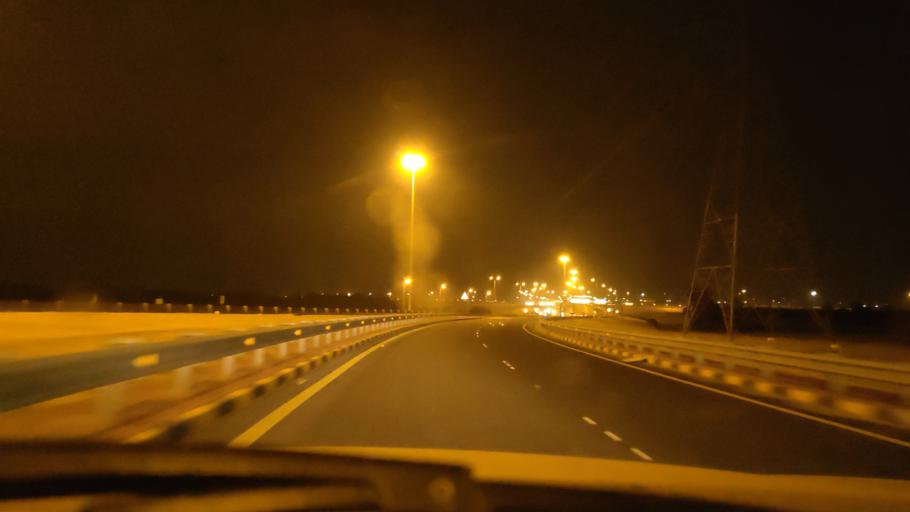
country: KW
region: Muhafazat al Jahra'
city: Al Jahra'
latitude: 29.2870
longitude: 47.7863
